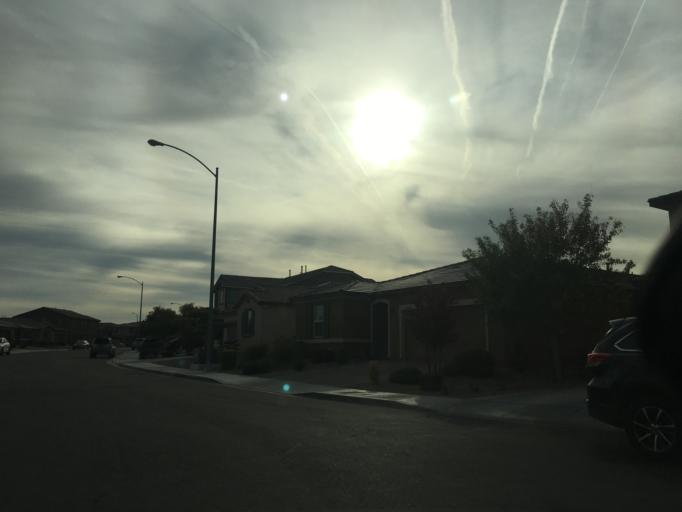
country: US
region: Nevada
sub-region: Clark County
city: Enterprise
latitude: 36.0166
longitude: -115.1652
